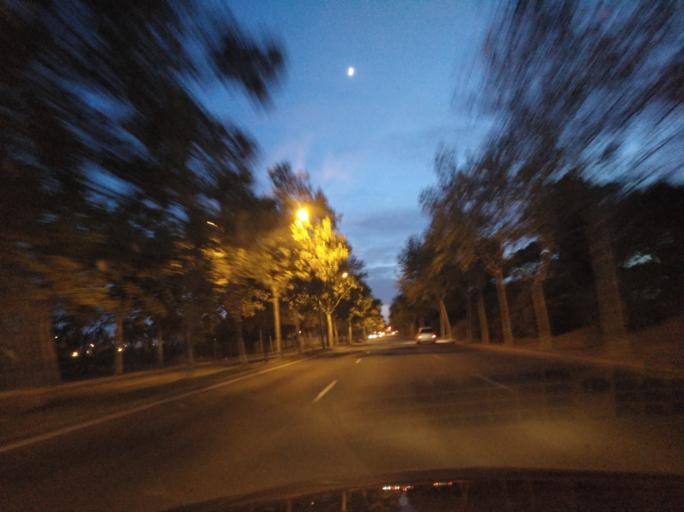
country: ES
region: Andalusia
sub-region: Provincia de Sevilla
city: Camas
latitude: 37.4016
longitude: -6.0111
